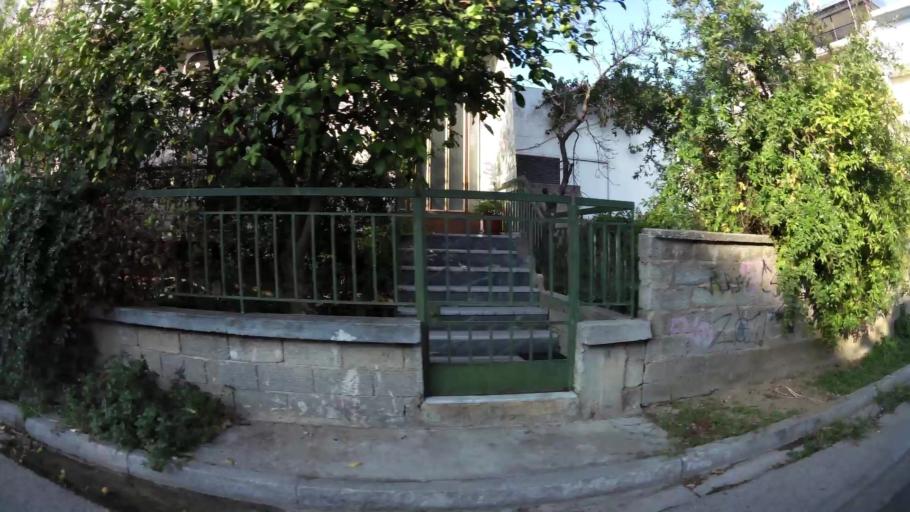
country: GR
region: Attica
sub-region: Nomarchia Anatolikis Attikis
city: Acharnes
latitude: 38.0855
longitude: 23.7309
